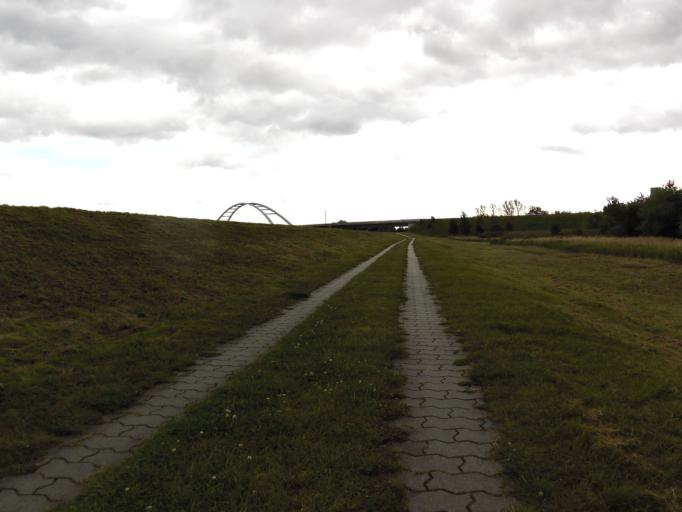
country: DE
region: Saxony-Anhalt
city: Tangermunde
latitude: 52.5687
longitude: 11.9803
